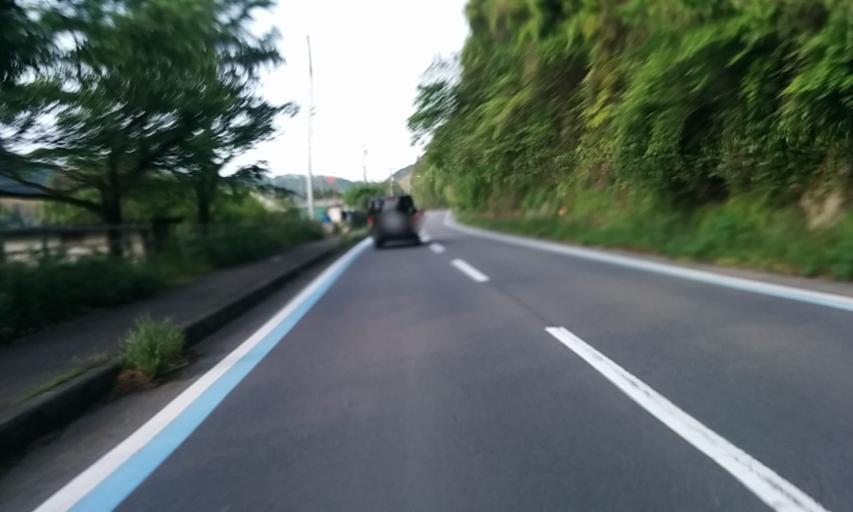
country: JP
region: Ehime
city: Saijo
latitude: 33.8787
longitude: 133.1756
